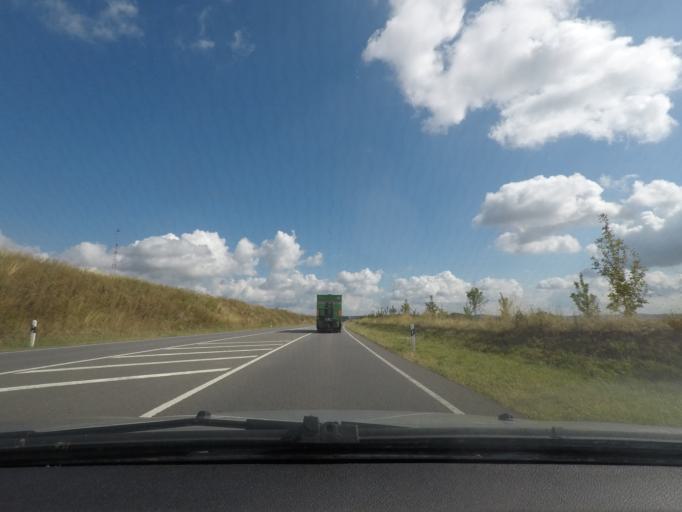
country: LU
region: Grevenmacher
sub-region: Canton de Grevenmacher
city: Junglinster
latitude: 49.7116
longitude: 6.2659
